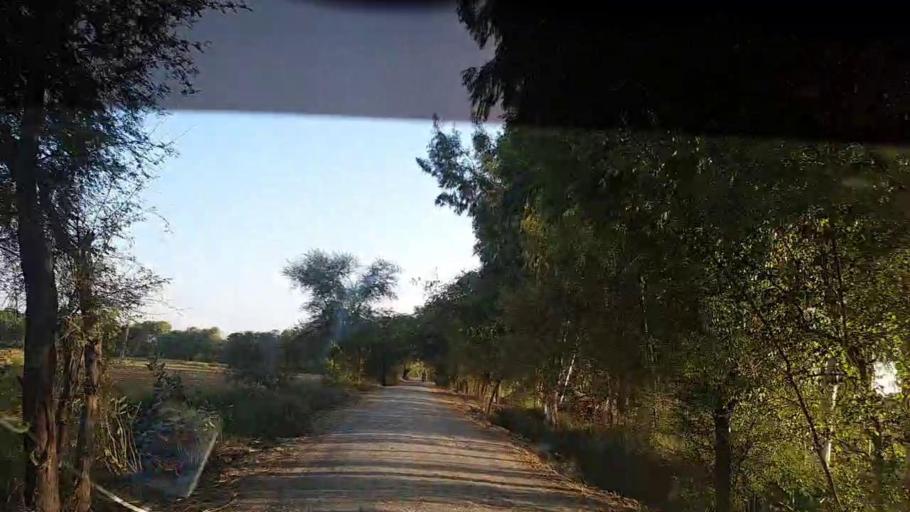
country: PK
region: Sindh
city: Ratodero
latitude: 27.8714
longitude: 68.1877
